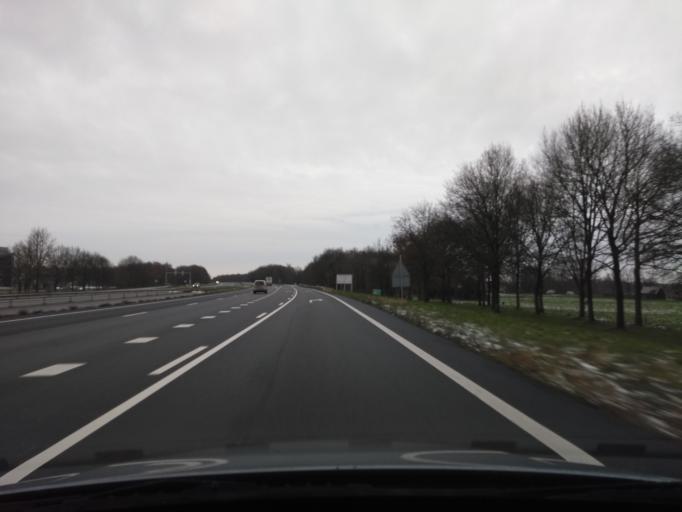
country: NL
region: Overijssel
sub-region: Gemeente Hengelo
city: Hengelo
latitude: 52.2432
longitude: 6.7575
